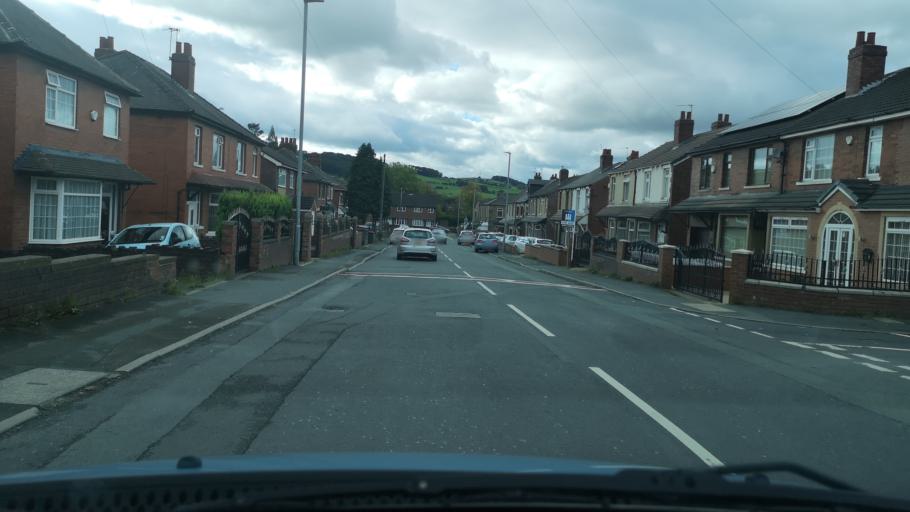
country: GB
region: England
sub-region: Kirklees
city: Dewsbury
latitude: 53.6747
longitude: -1.6284
